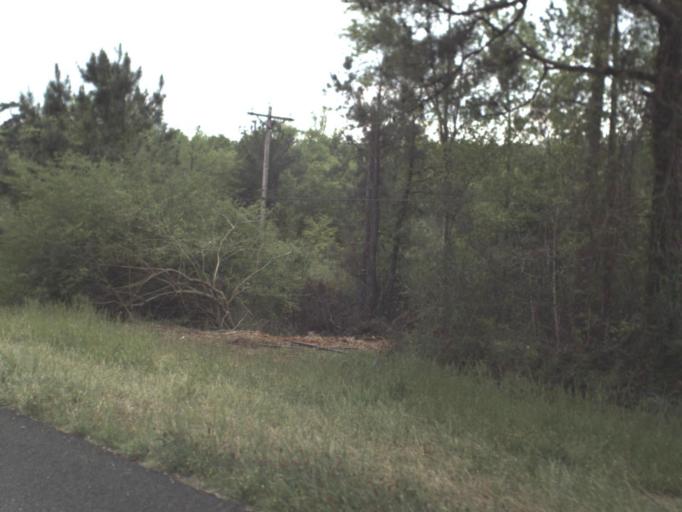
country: US
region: Florida
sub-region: Escambia County
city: Century
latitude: 30.9203
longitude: -87.3137
